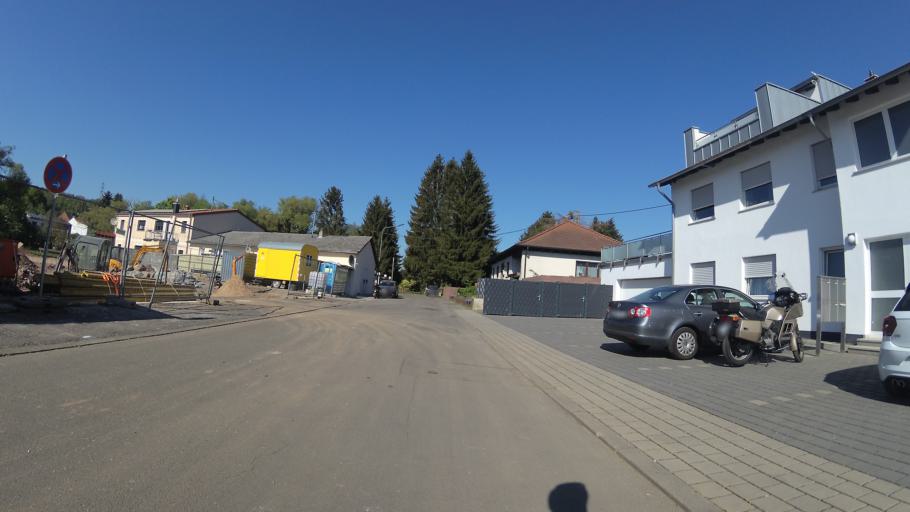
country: DE
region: Saarland
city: Hangard
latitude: 49.3714
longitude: 7.1921
